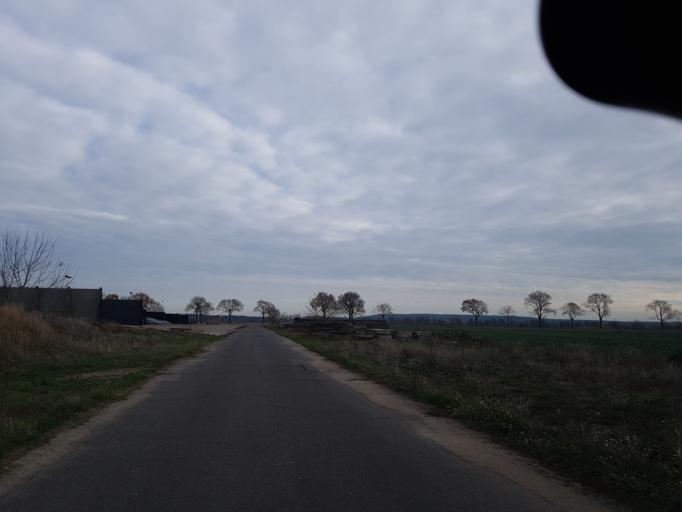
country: DE
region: Brandenburg
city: Treuenbrietzen
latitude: 52.0914
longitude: 12.9431
